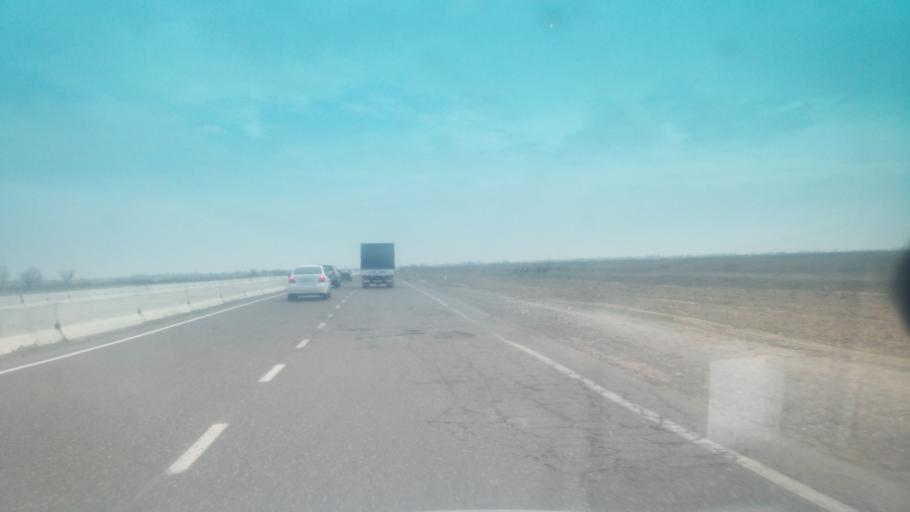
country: KZ
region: Ongtustik Qazaqstan
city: Myrzakent
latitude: 40.5130
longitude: 68.4904
